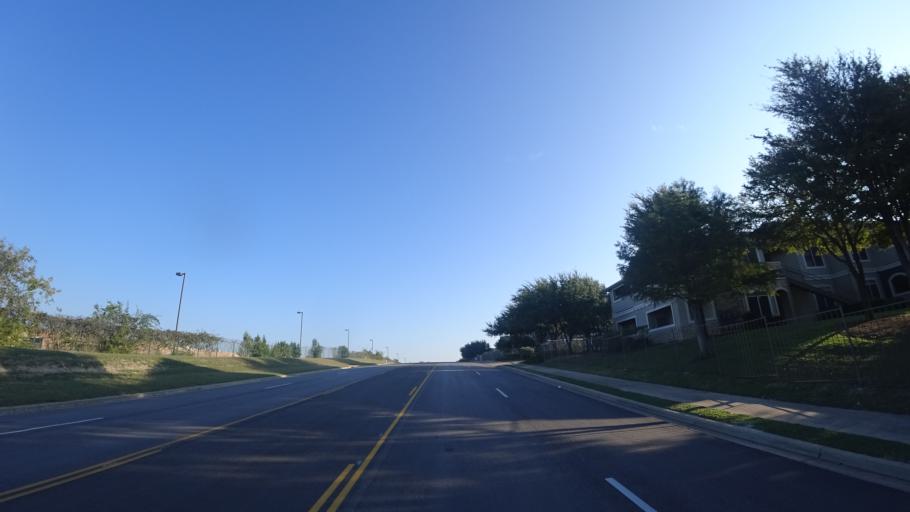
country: US
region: Texas
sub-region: Travis County
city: Austin
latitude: 30.3317
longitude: -97.6656
